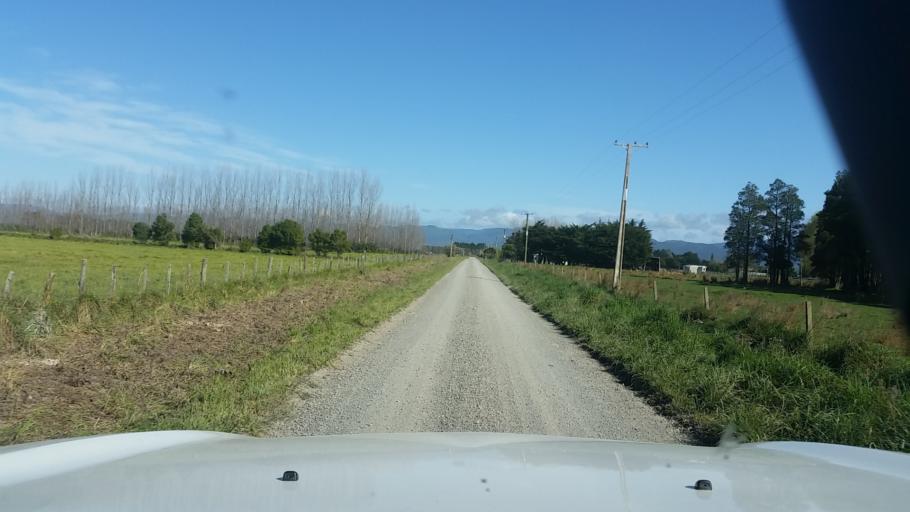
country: NZ
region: Wellington
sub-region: South Wairarapa District
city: Waipawa
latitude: -41.1431
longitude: 175.4131
